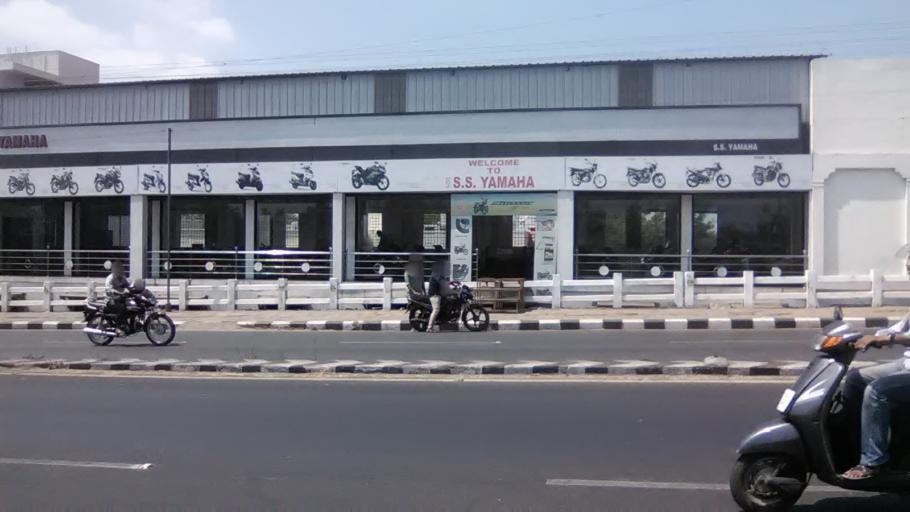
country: IN
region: Tamil Nadu
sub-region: Tiruchchirappalli
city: Tiruchirappalli
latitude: 10.7946
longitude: 78.6936
